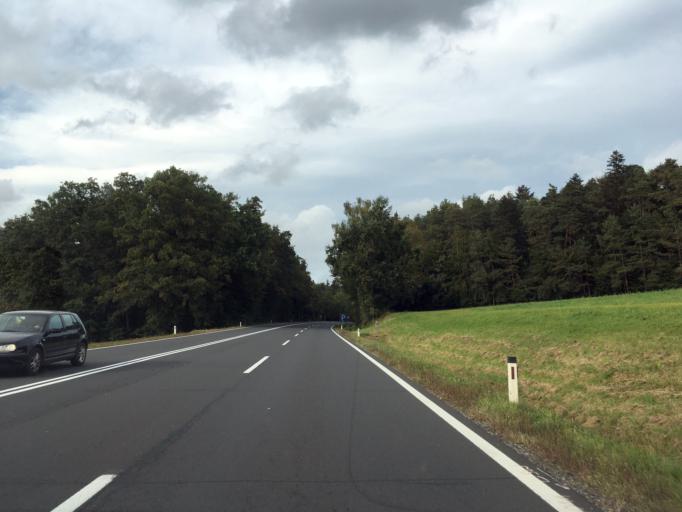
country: AT
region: Styria
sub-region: Politischer Bezirk Hartberg-Fuerstenfeld
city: Grafendorf bei Hartberg
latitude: 47.3484
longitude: 16.0100
